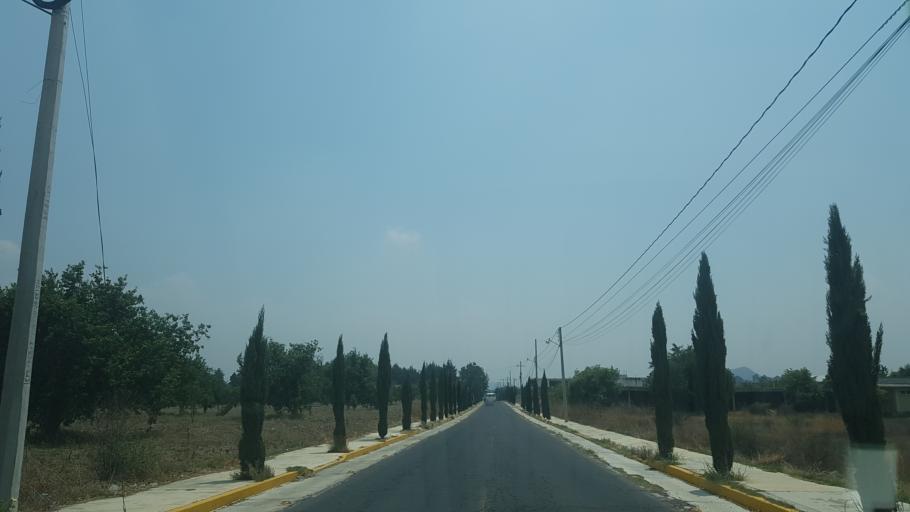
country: MX
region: Puebla
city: San Andres Calpan
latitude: 19.1024
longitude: -98.4443
